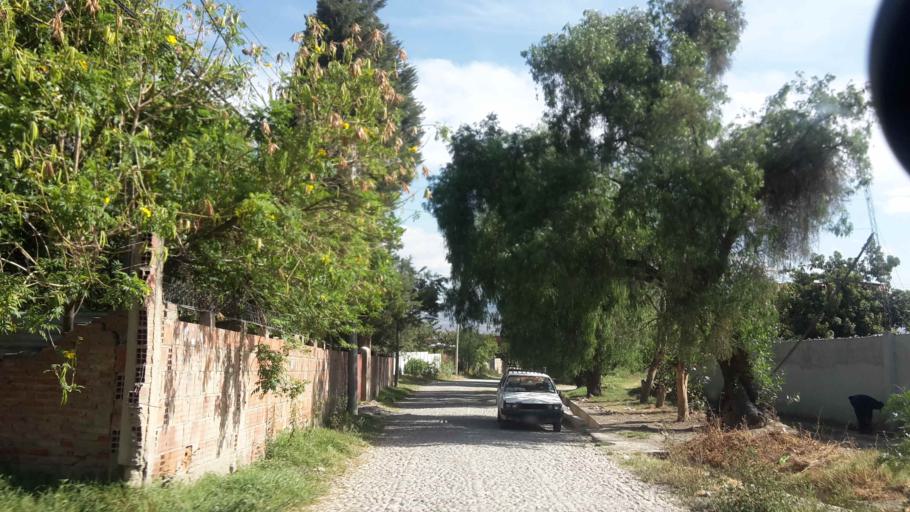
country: BO
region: Cochabamba
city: Cochabamba
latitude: -17.3504
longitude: -66.1978
